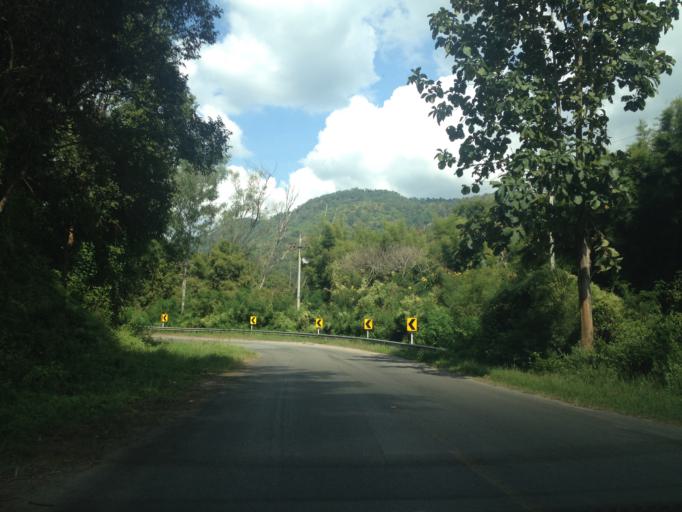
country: TH
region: Chiang Mai
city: Samoeng
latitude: 18.8019
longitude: 98.8309
